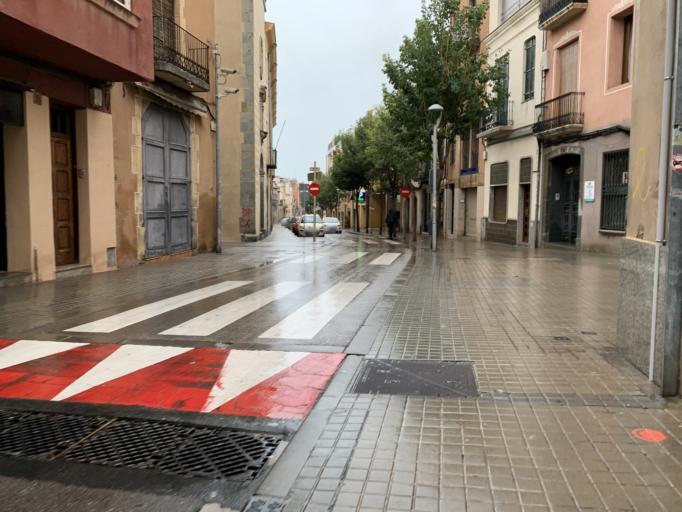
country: ES
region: Catalonia
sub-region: Provincia de Barcelona
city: Mataro
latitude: 41.5400
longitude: 2.4486
